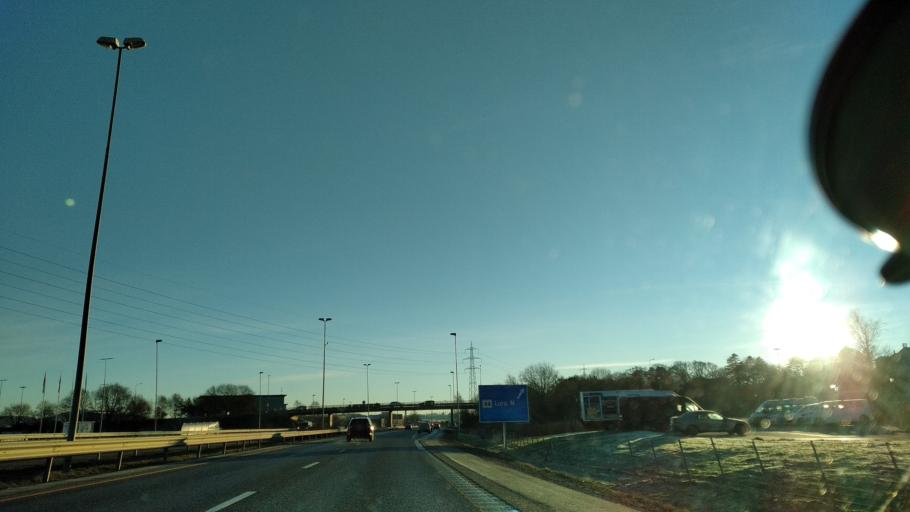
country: NO
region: Rogaland
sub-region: Sandnes
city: Sandnes
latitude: 58.8882
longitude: 5.7168
